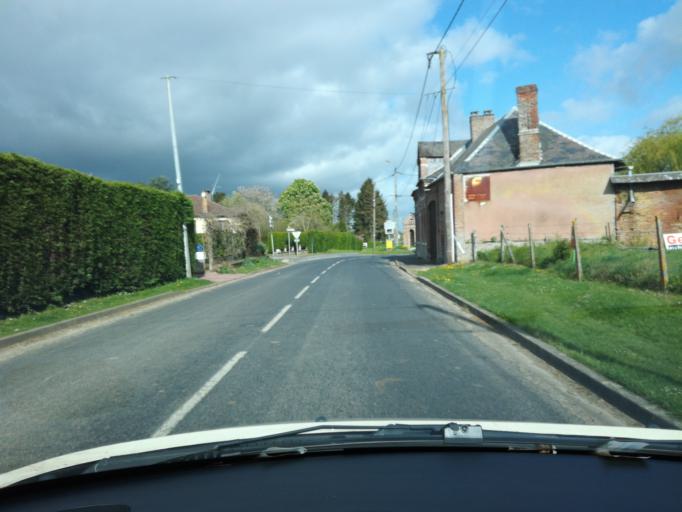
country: FR
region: Picardie
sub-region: Departement de la Somme
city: Beaucamps-le-Vieux
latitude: 49.8710
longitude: 1.8284
